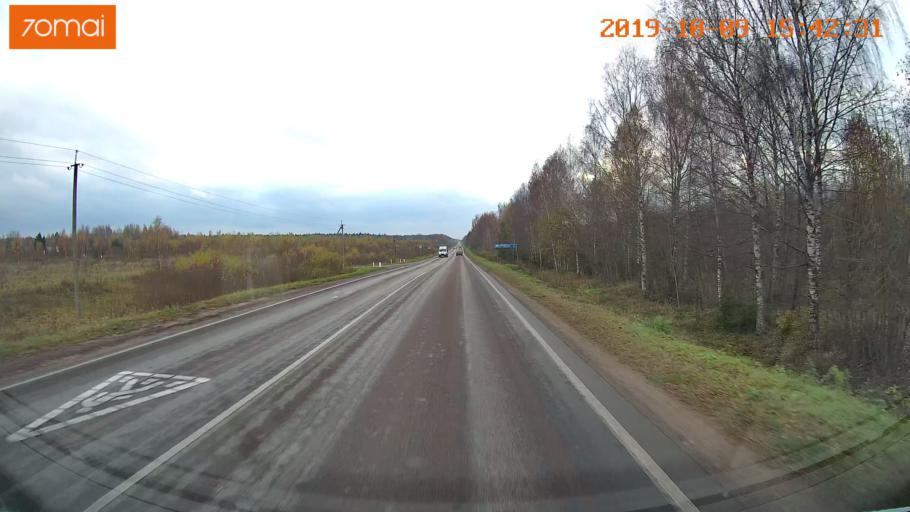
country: RU
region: Kostroma
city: Oktyabr'skiy
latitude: 57.8675
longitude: 41.1053
